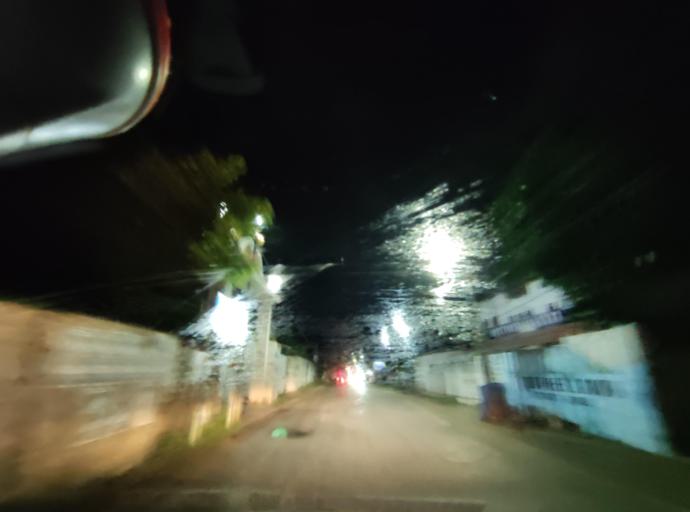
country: IN
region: Kerala
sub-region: Thiruvananthapuram
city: Thiruvananthapuram
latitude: 8.4726
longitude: 76.9219
